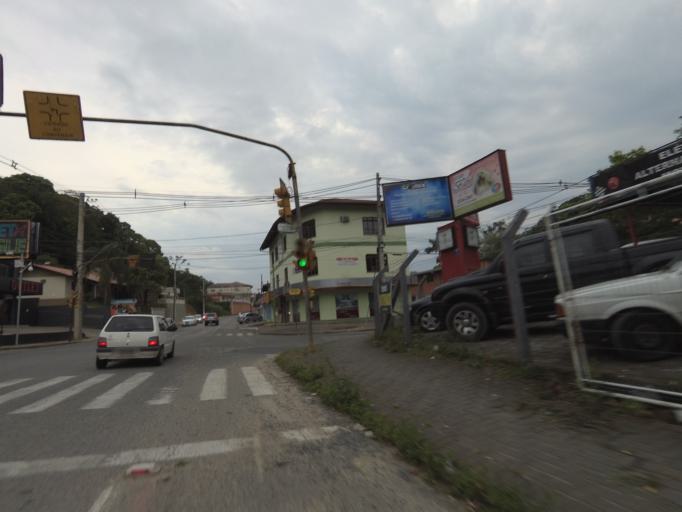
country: BR
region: Santa Catarina
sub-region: Blumenau
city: Blumenau
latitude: -26.8625
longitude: -49.0531
